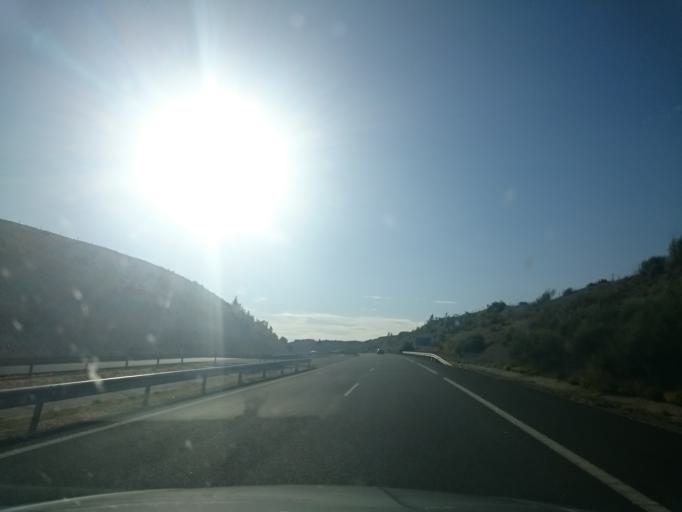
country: ES
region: Castille and Leon
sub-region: Provincia de Burgos
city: Villanueva de Argano
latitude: 42.3783
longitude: -3.9359
